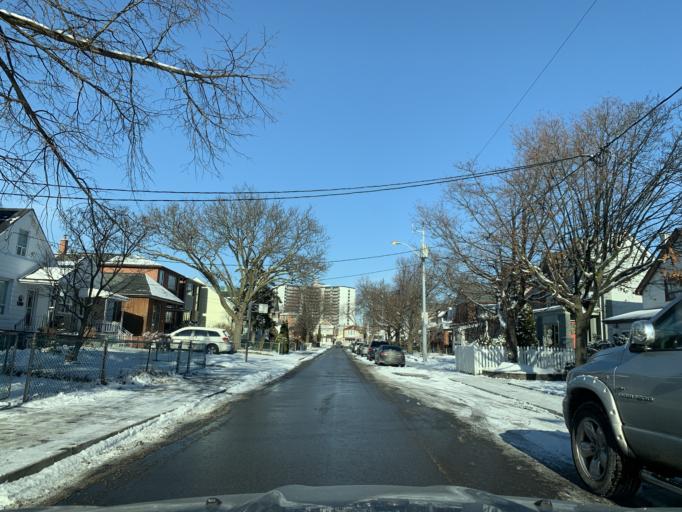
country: CA
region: Ontario
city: Toronto
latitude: 43.6688
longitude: -79.4888
